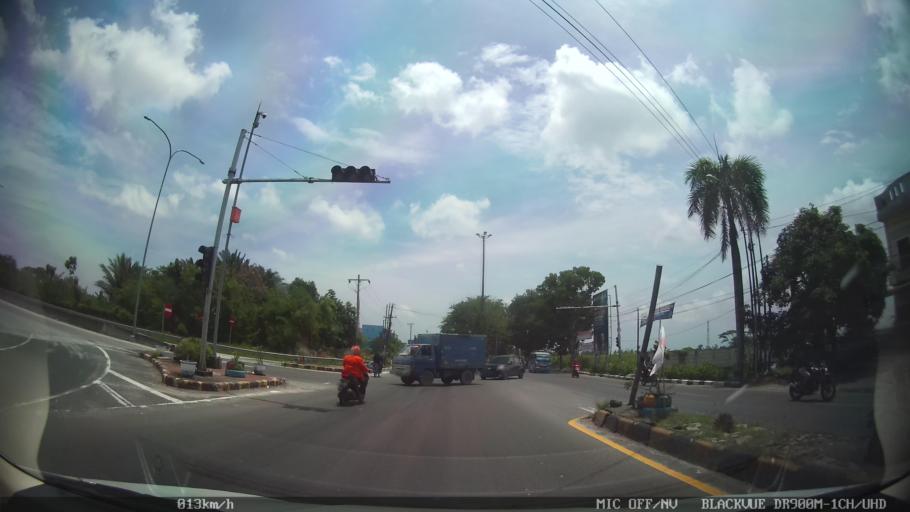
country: ID
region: North Sumatra
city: Percut
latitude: 3.5524
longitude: 98.8542
